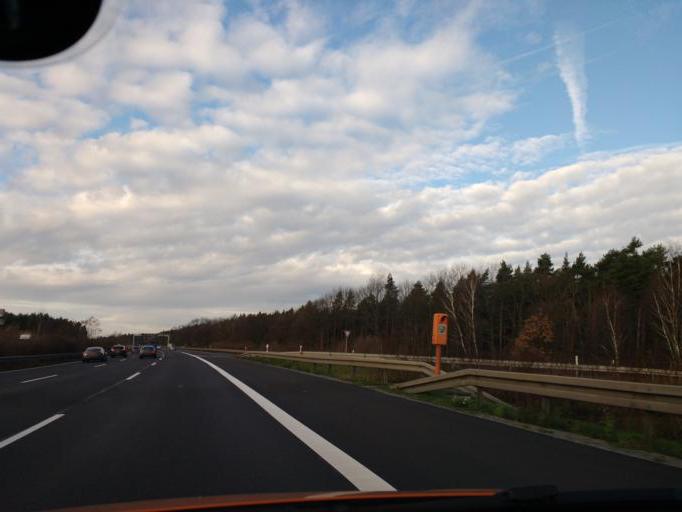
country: DE
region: Lower Saxony
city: Mariental
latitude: 52.2639
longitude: 10.9837
